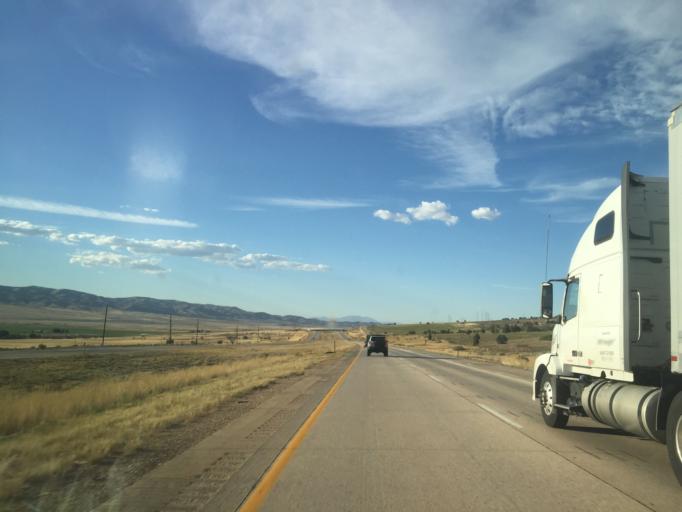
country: US
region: Utah
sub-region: Juab County
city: Nephi
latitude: 39.7343
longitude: -111.8257
